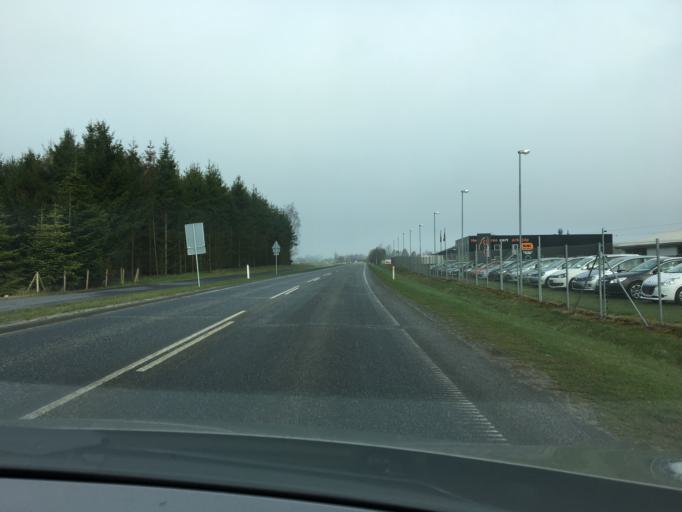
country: DK
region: South Denmark
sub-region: Vejle Kommune
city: Give
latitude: 55.8202
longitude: 9.3403
